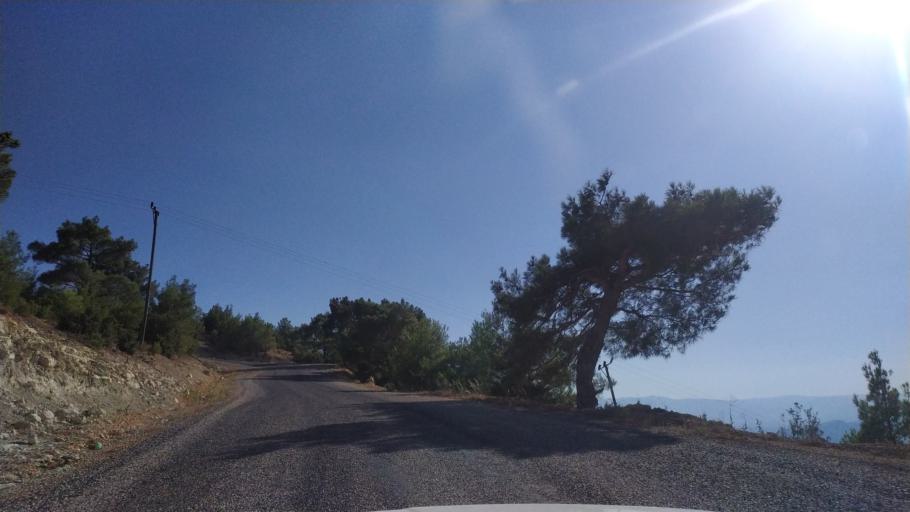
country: TR
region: Mersin
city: Mut
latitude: 36.7030
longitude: 33.4748
